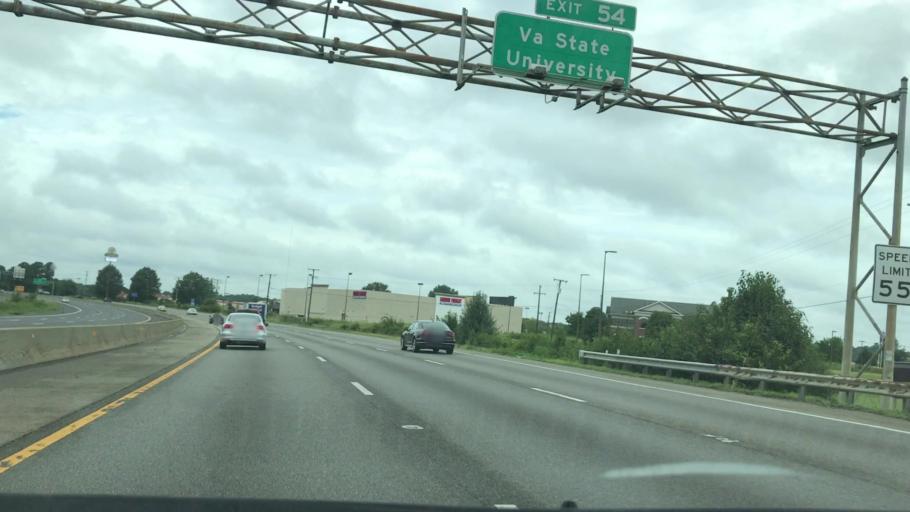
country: US
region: Virginia
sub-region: City of Petersburg
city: Petersburg
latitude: 37.2475
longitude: -77.3930
